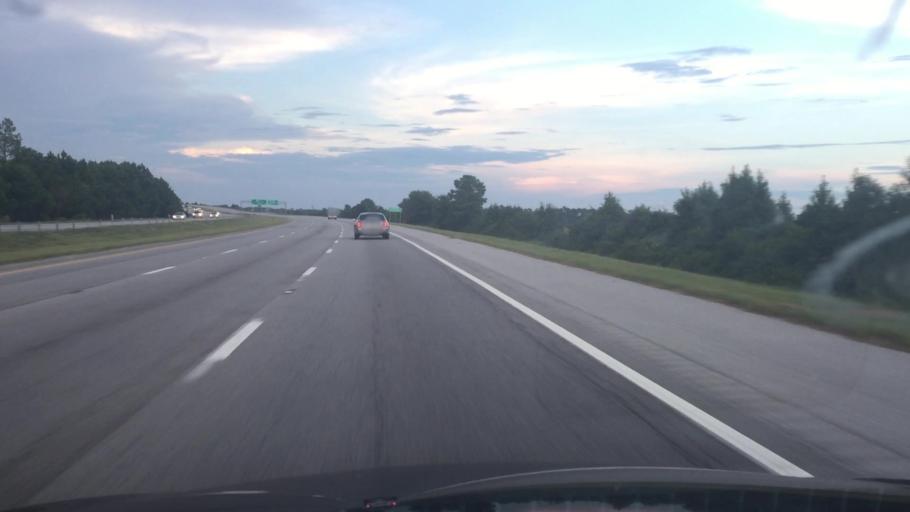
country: US
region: South Carolina
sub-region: Horry County
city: North Myrtle Beach
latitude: 33.8366
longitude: -78.7085
